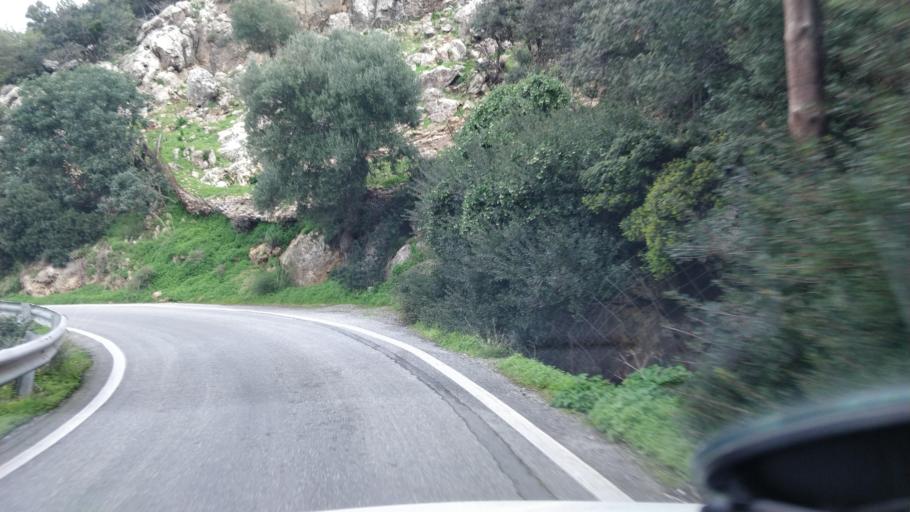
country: GR
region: Crete
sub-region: Nomos Lasithiou
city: Agios Nikolaos
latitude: 35.1091
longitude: 25.7160
